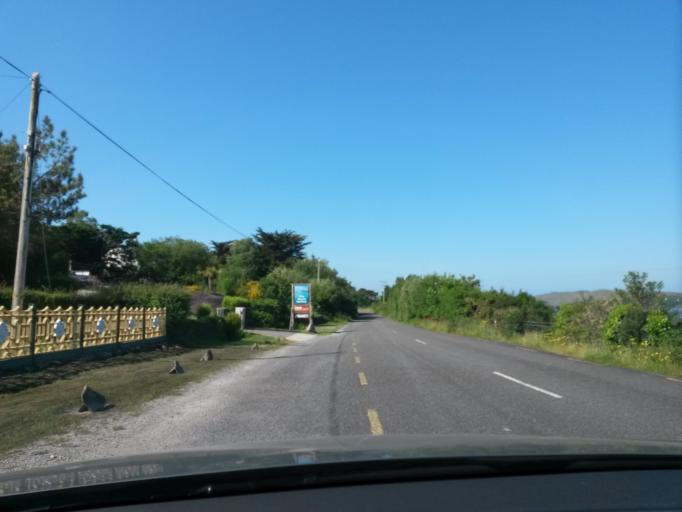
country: IE
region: Munster
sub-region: Ciarrai
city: Kenmare
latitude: 51.7551
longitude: -9.8475
